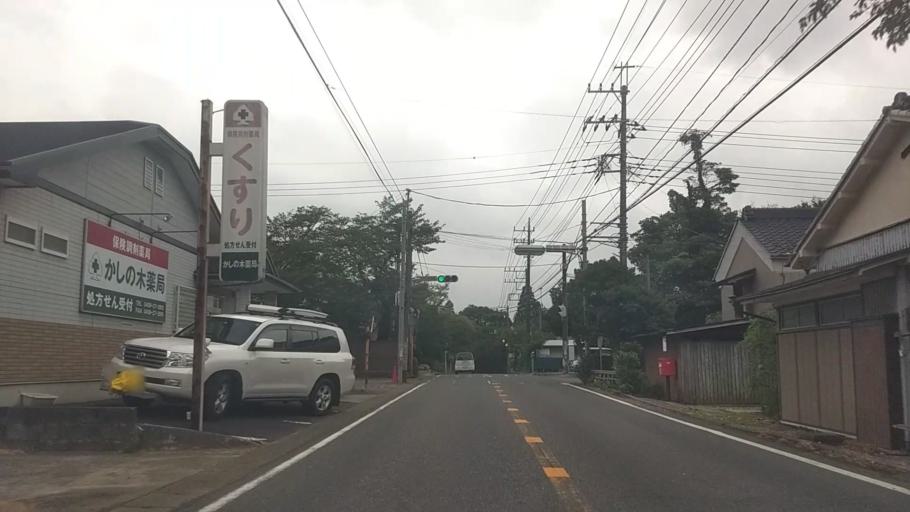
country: JP
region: Chiba
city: Kisarazu
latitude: 35.3018
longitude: 140.0729
